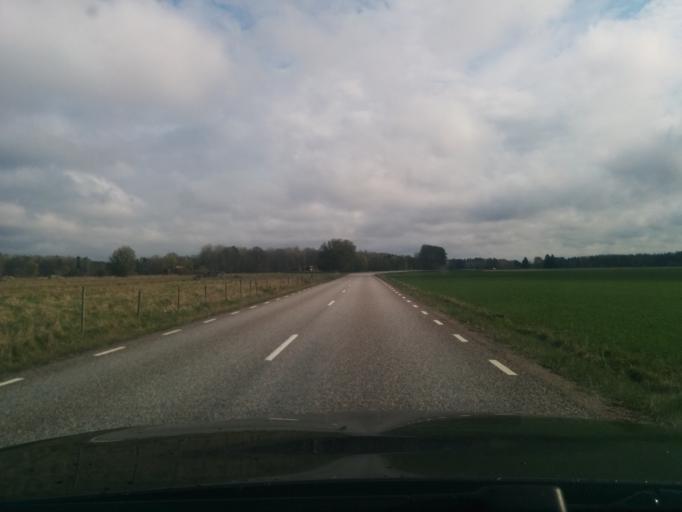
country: SE
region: Uppsala
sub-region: Tierps Kommun
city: Orbyhus
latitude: 60.1804
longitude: 17.6630
